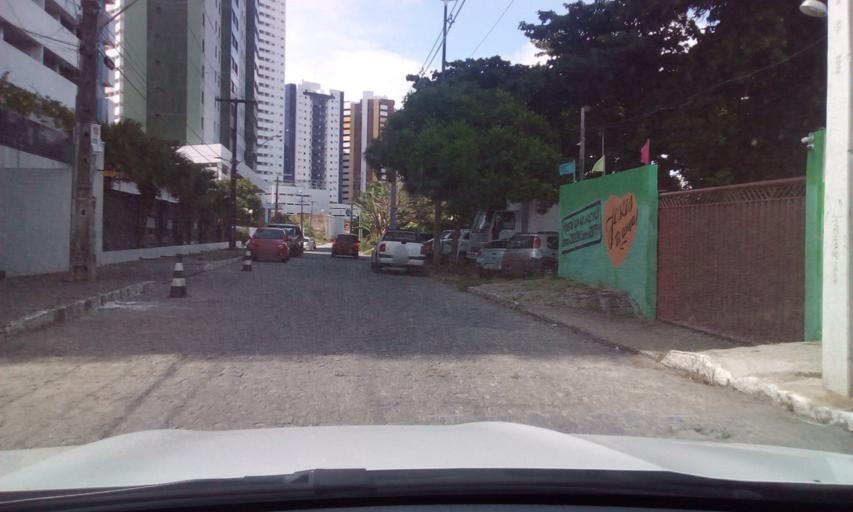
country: BR
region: Paraiba
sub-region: Joao Pessoa
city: Joao Pessoa
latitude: -7.1190
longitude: -34.8332
